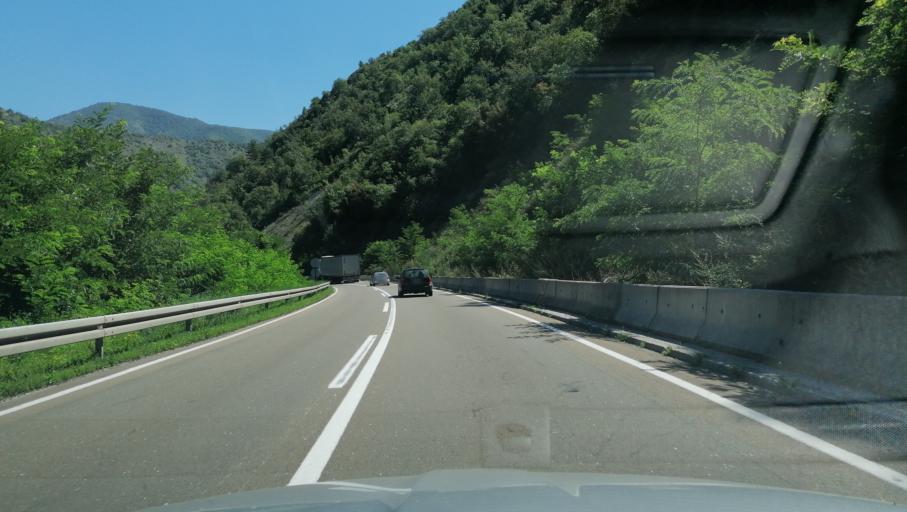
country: RS
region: Central Serbia
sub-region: Raski Okrug
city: Kraljevo
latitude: 43.5611
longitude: 20.6097
